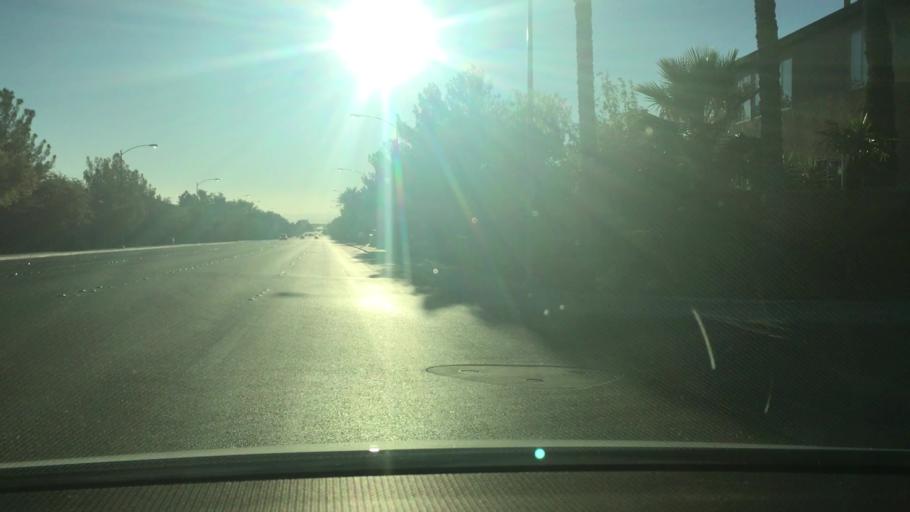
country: US
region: Nevada
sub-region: Clark County
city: Summerlin South
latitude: 36.0775
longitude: -115.3137
